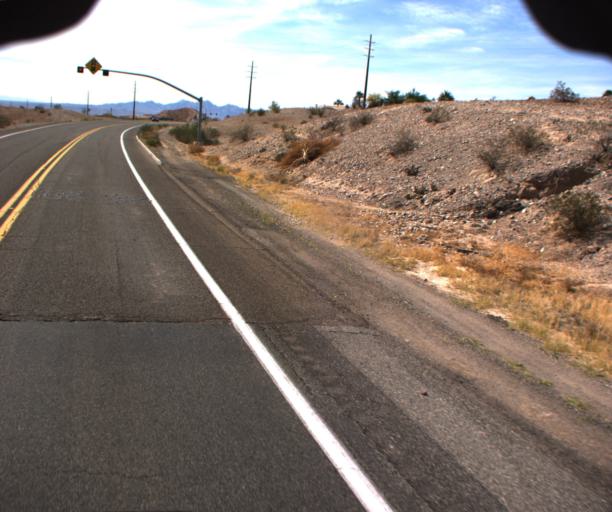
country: US
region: Arizona
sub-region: Mohave County
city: Lake Havasu City
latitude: 34.4512
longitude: -114.2618
